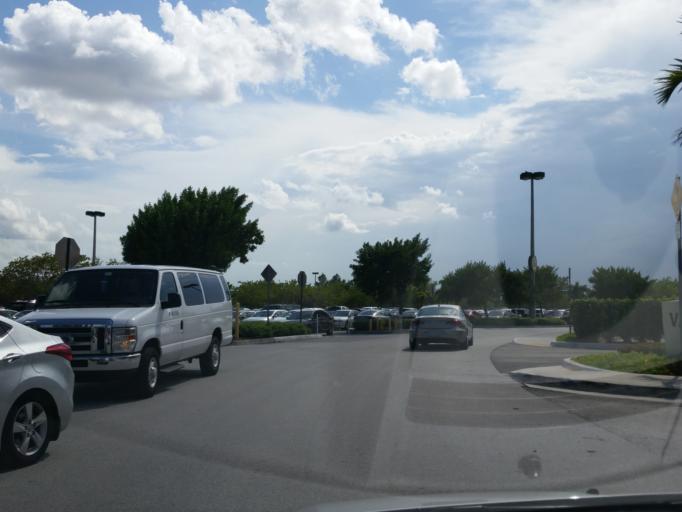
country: US
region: Florida
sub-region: Miami-Dade County
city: Sweetwater
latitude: 25.7859
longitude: -80.3798
